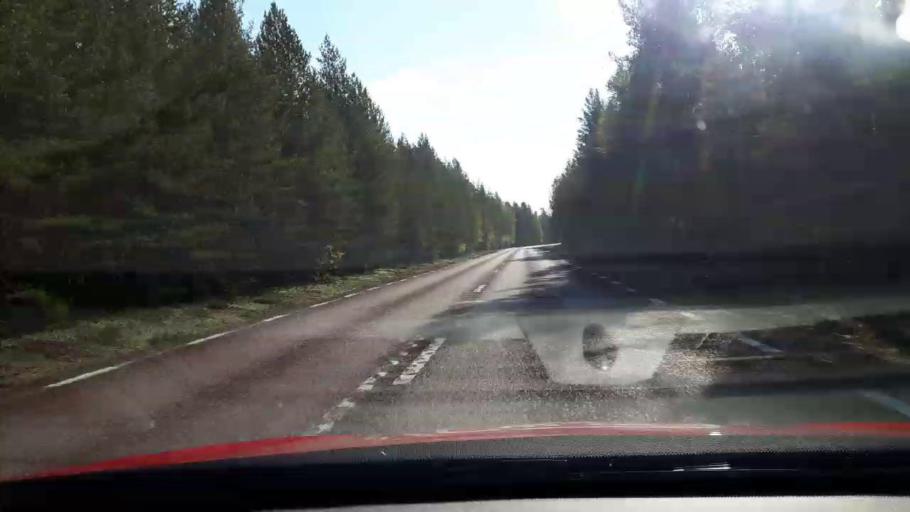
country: SE
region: Gaevleborg
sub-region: Ljusdals Kommun
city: Farila
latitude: 61.9062
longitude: 15.6334
